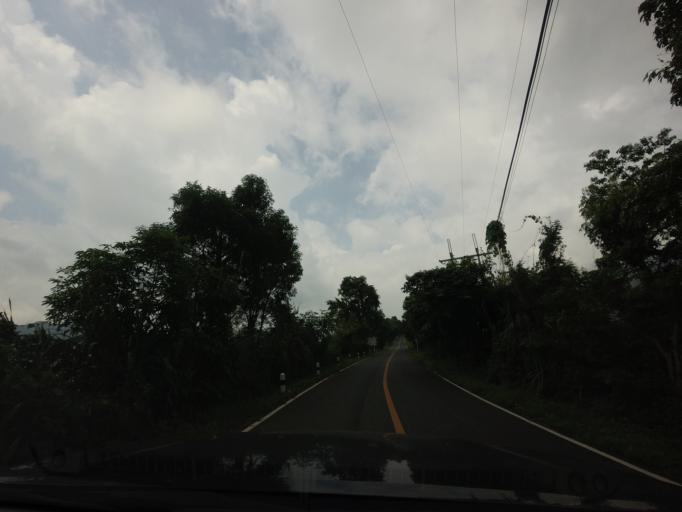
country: TH
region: Nan
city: Bo Kluea
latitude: 19.1965
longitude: 101.0530
